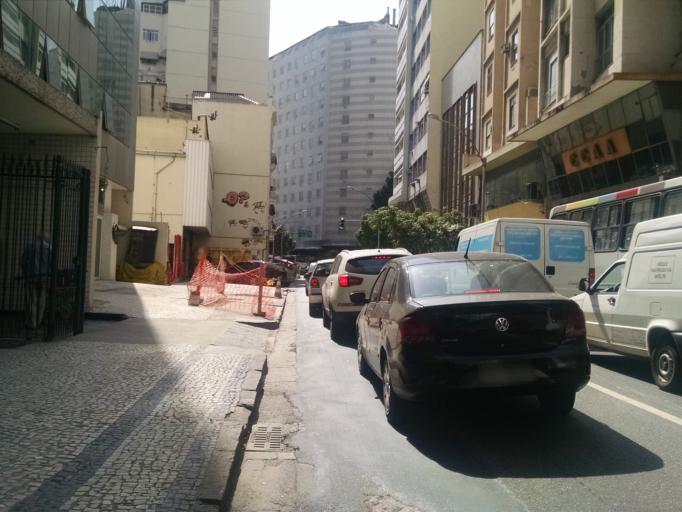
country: BR
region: Rio de Janeiro
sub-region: Rio De Janeiro
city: Rio de Janeiro
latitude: -22.9147
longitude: -43.1892
